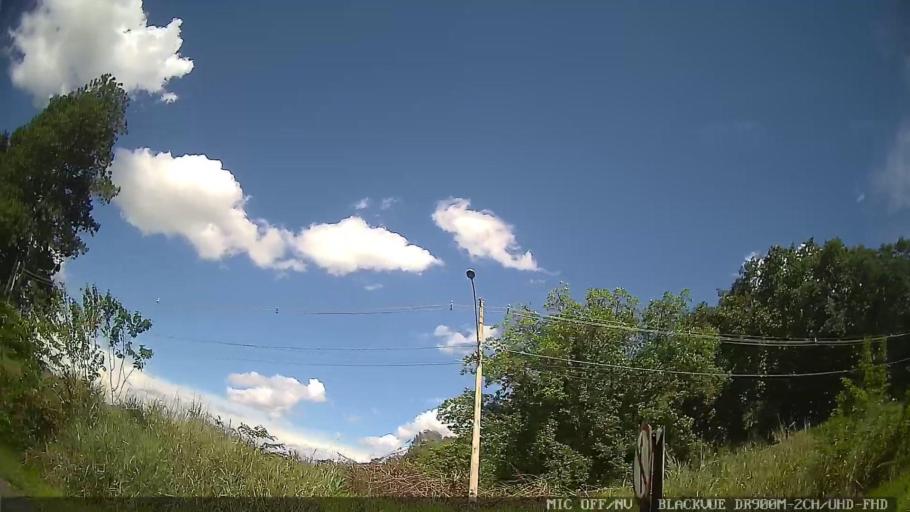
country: BR
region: Sao Paulo
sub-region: Pedreira
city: Pedreira
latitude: -22.7257
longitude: -46.8522
